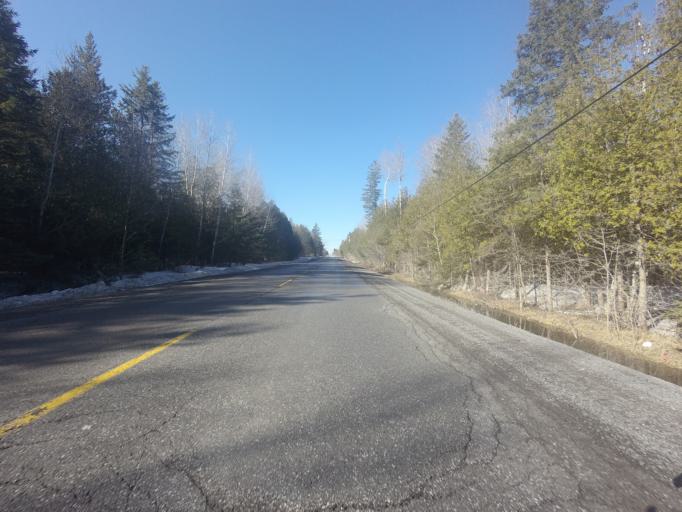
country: CA
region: Ontario
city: Bells Corners
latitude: 45.2322
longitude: -75.9373
